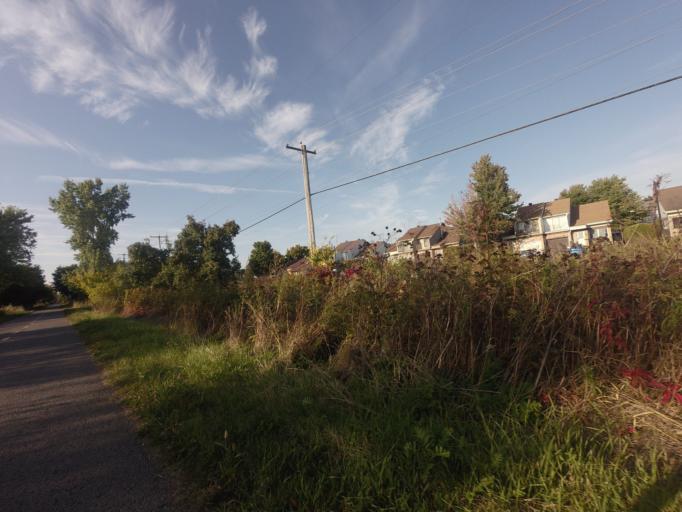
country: CA
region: Quebec
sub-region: Laurentides
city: Saint-Jerome
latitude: 45.7983
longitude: -74.0035
